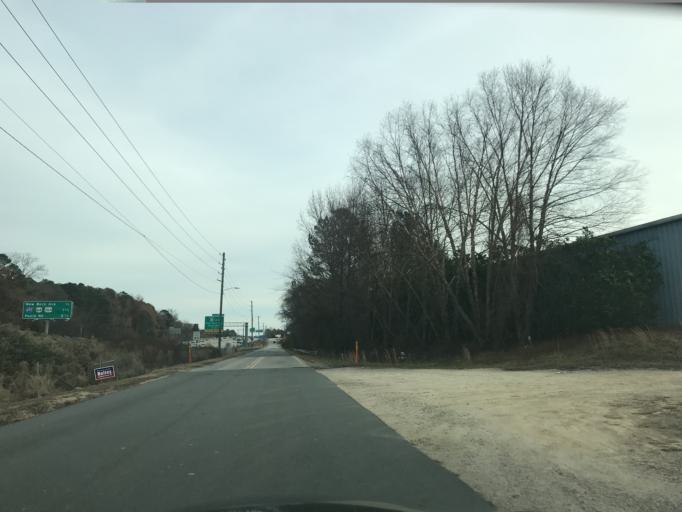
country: US
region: North Carolina
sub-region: Wake County
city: Raleigh
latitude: 35.8002
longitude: -78.5916
